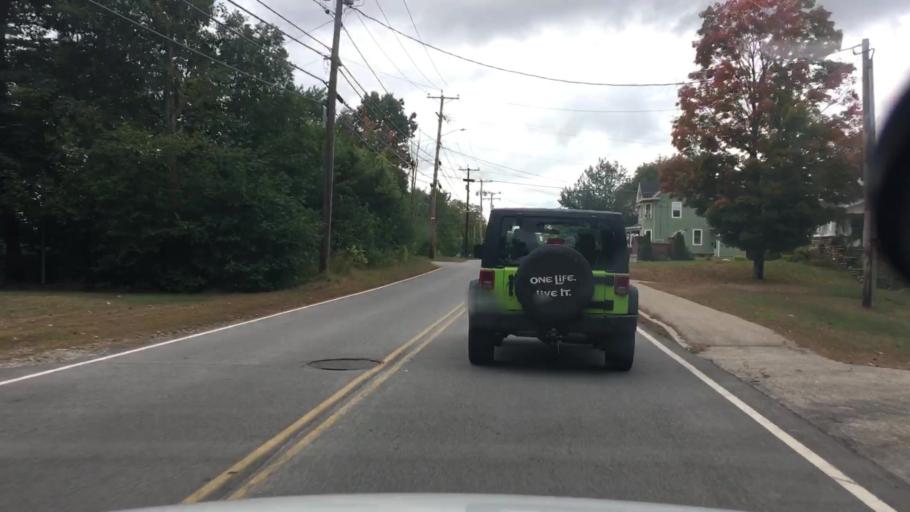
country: US
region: New Hampshire
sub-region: Strafford County
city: Rochester
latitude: 43.2922
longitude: -70.9709
